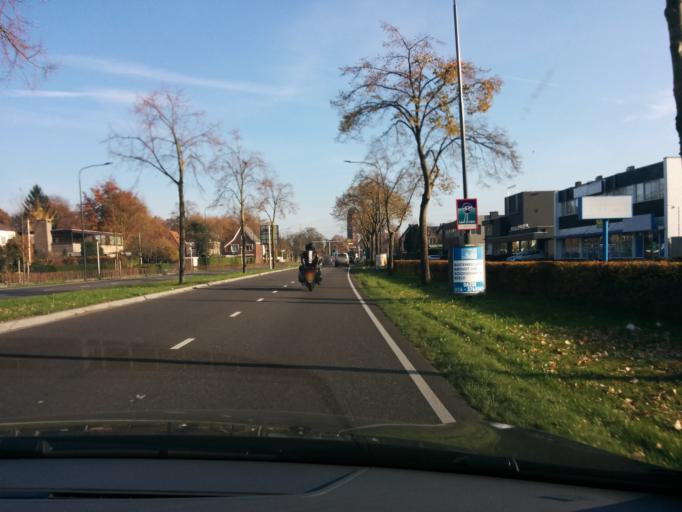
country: NL
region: North Brabant
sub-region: Gemeente Helmond
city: Helmond
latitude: 51.4756
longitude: 5.6362
